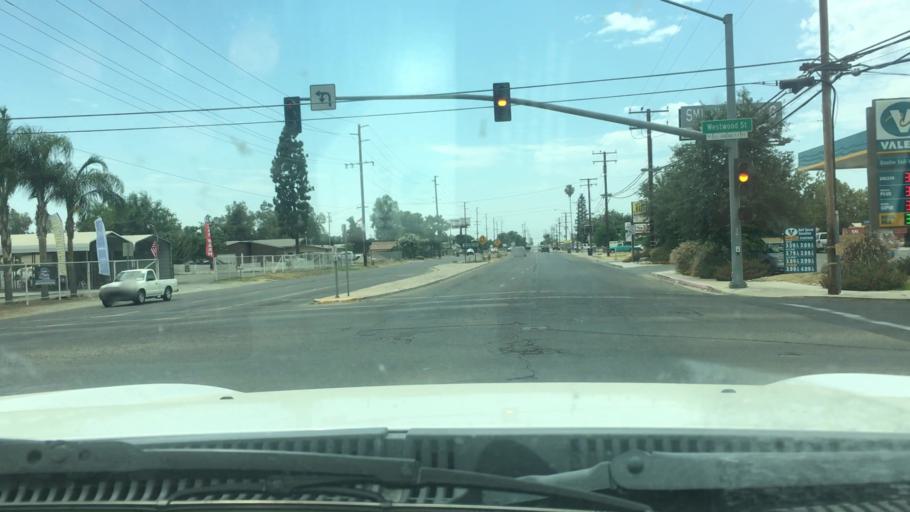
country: US
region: California
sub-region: Tulare County
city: Porterville
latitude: 36.0658
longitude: -119.0708
